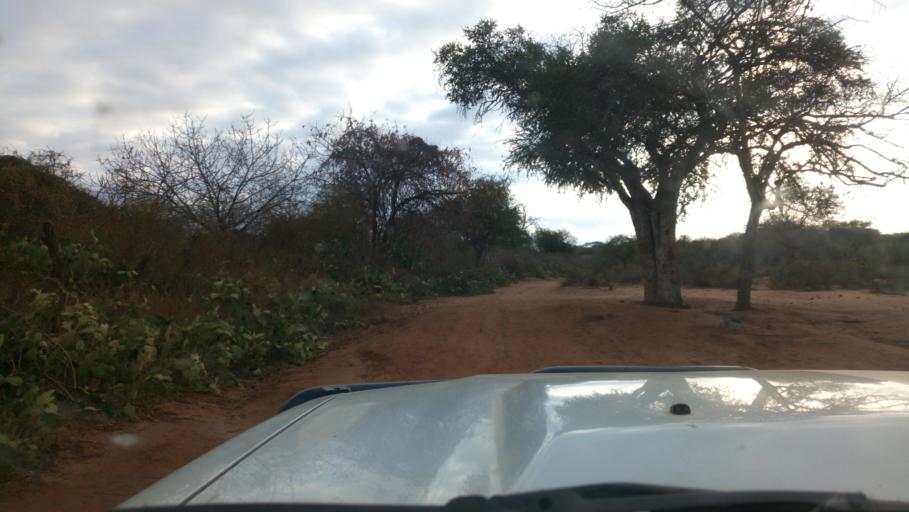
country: KE
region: Kitui
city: Kitui
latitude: -1.8889
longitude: 38.2356
